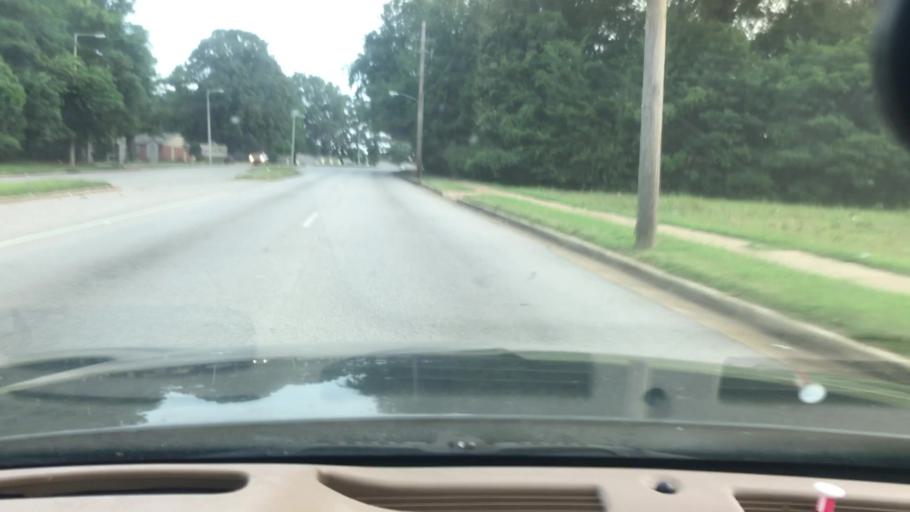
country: US
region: Tennessee
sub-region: Shelby County
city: Bartlett
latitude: 35.1749
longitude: -89.8704
